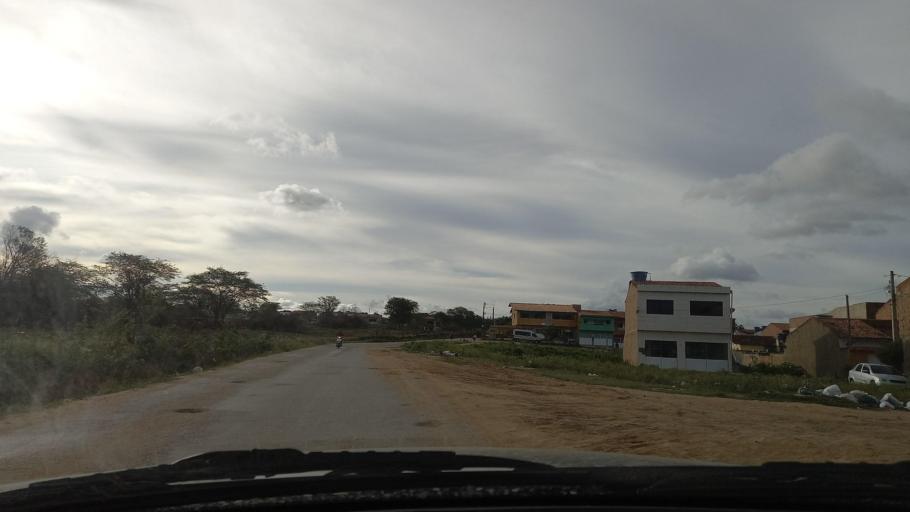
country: BR
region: Pernambuco
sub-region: Gravata
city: Gravata
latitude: -8.2045
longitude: -35.5596
